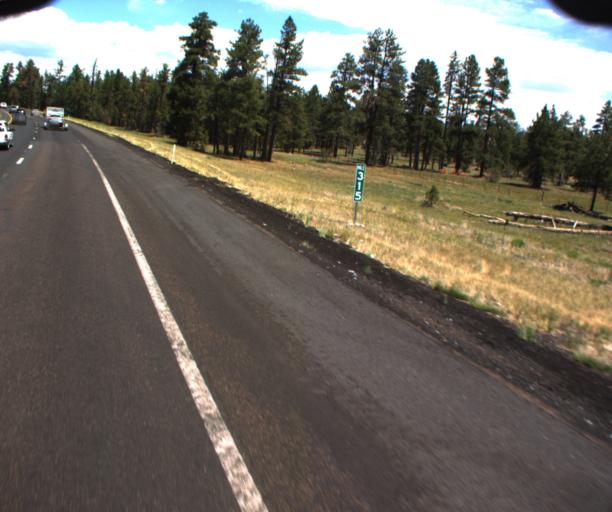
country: US
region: Arizona
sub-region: Coconino County
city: Sedona
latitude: 34.8451
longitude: -111.6035
